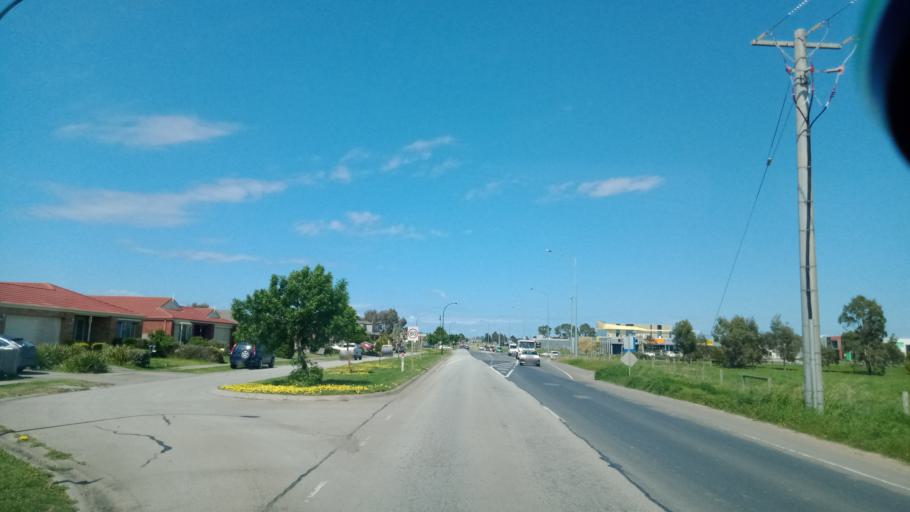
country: AU
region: Victoria
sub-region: Casey
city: Cranbourne West
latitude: -38.0899
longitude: 145.2563
